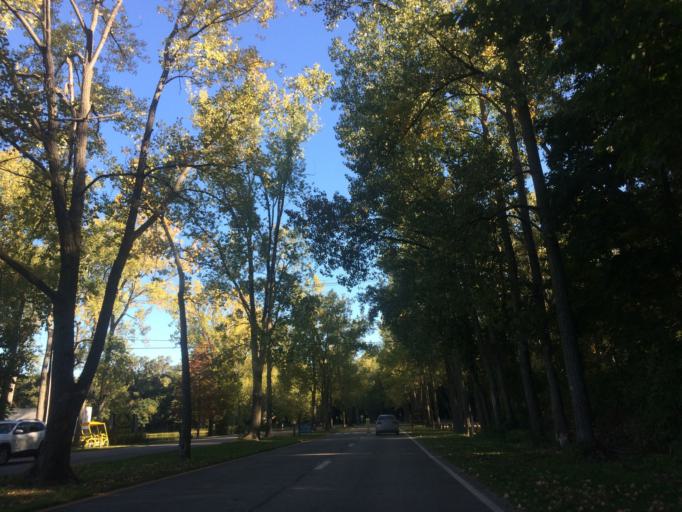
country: US
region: Pennsylvania
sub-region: Erie County
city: Erie
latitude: 42.1477
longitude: -80.1318
